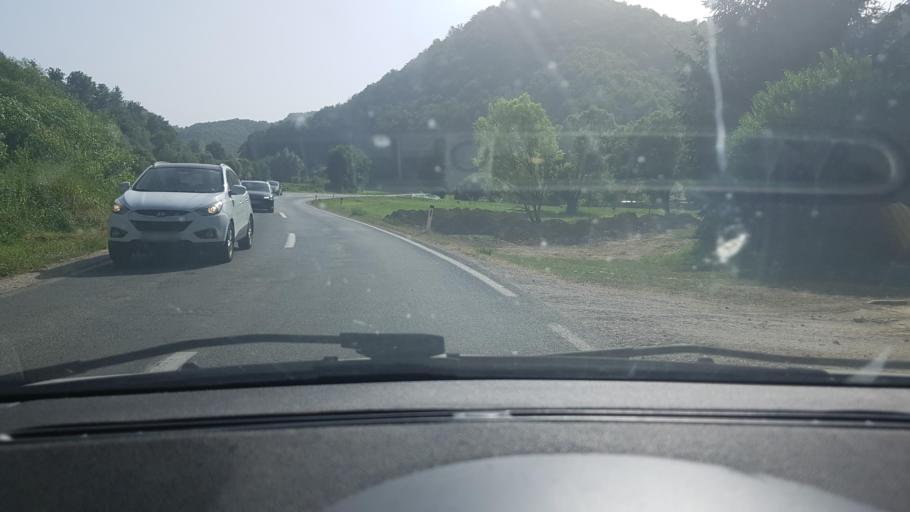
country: SI
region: Rogatec
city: Rogatec
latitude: 46.2223
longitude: 15.7409
